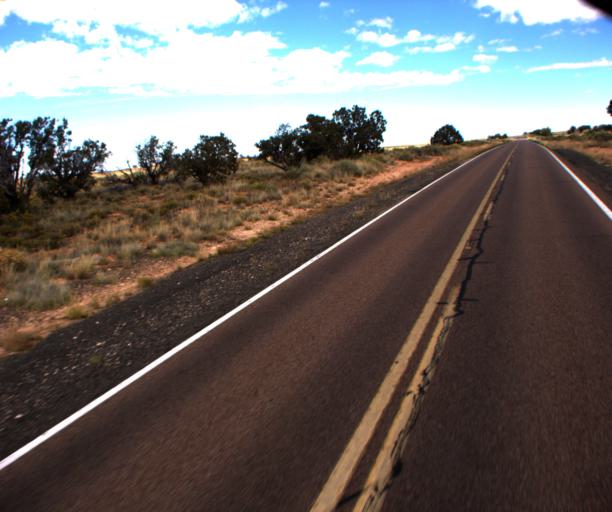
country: US
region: Arizona
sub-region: Navajo County
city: Snowflake
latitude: 34.6600
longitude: -110.3313
